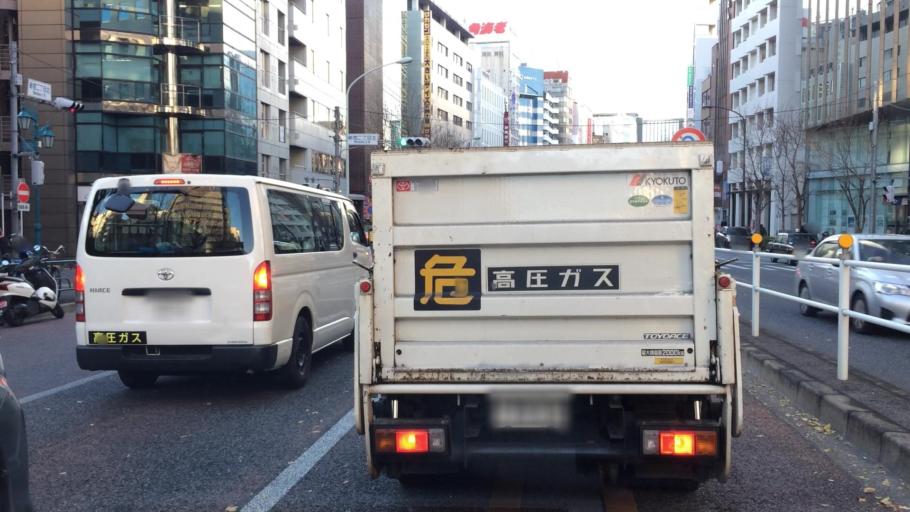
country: JP
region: Tokyo
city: Tokyo
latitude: 35.6916
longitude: 139.7093
